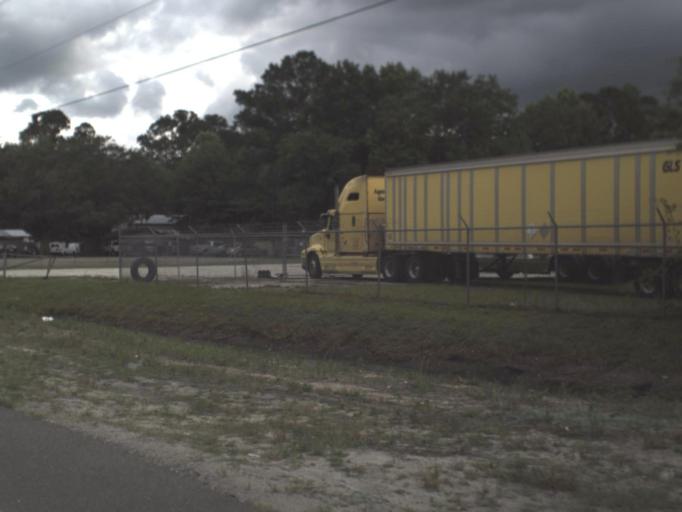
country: US
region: Florida
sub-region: Duval County
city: Jacksonville
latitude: 30.4037
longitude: -81.7425
